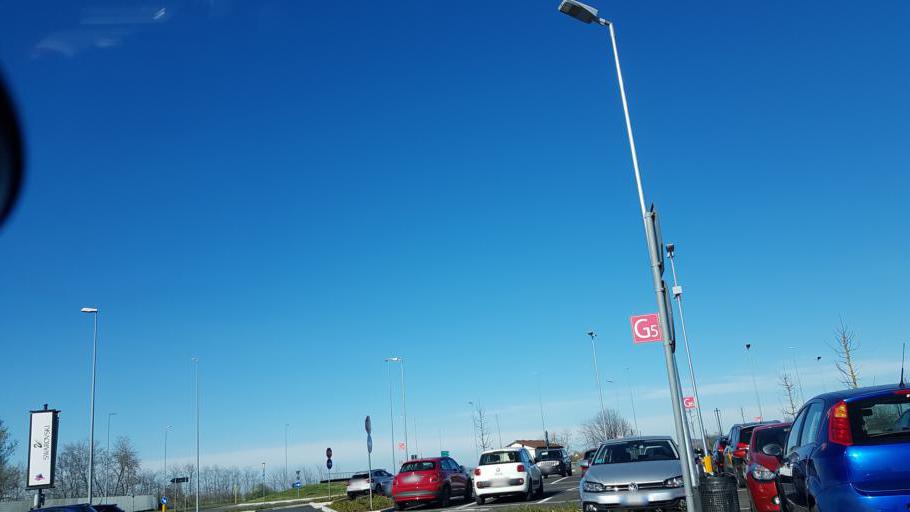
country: IT
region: Piedmont
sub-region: Provincia di Alessandria
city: Serravalle Scrivia
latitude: 44.7373
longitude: 8.8346
